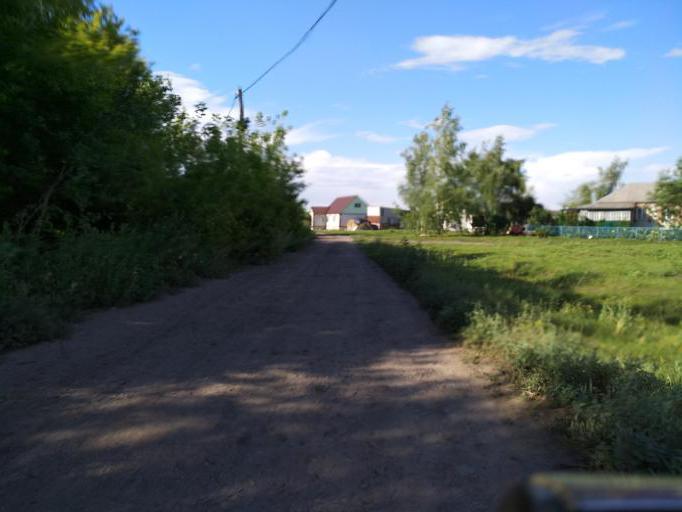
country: RU
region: Lipetsk
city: Dobrinka
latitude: 52.0297
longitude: 40.5626
